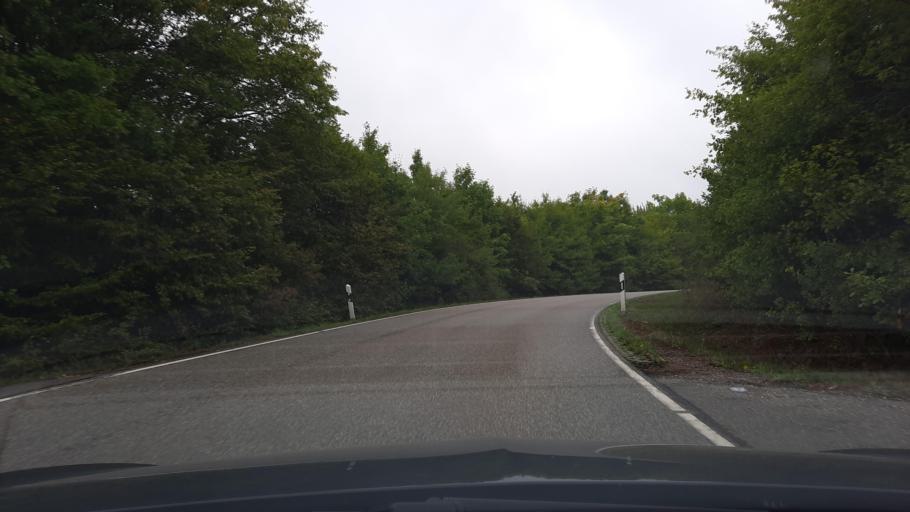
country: DE
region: Rheinland-Pfalz
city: Mertesdorf
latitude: 49.7696
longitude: 6.7434
